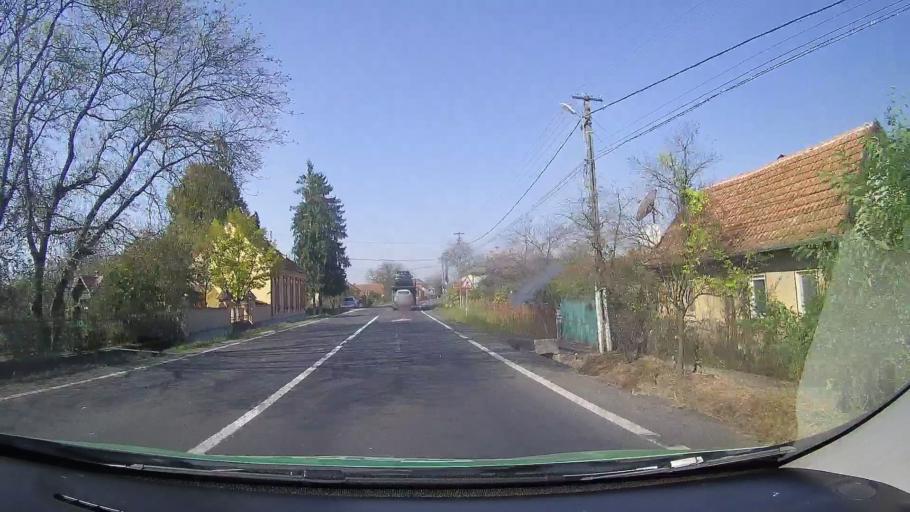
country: RO
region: Arad
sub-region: Comuna Varadia de Mures
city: Varadia de Mures
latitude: 46.0034
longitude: 22.1596
